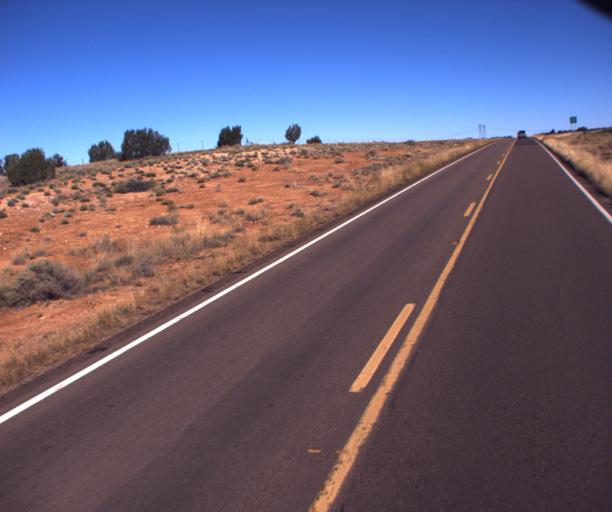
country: US
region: Arizona
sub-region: Navajo County
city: Snowflake
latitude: 34.6202
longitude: -110.0921
